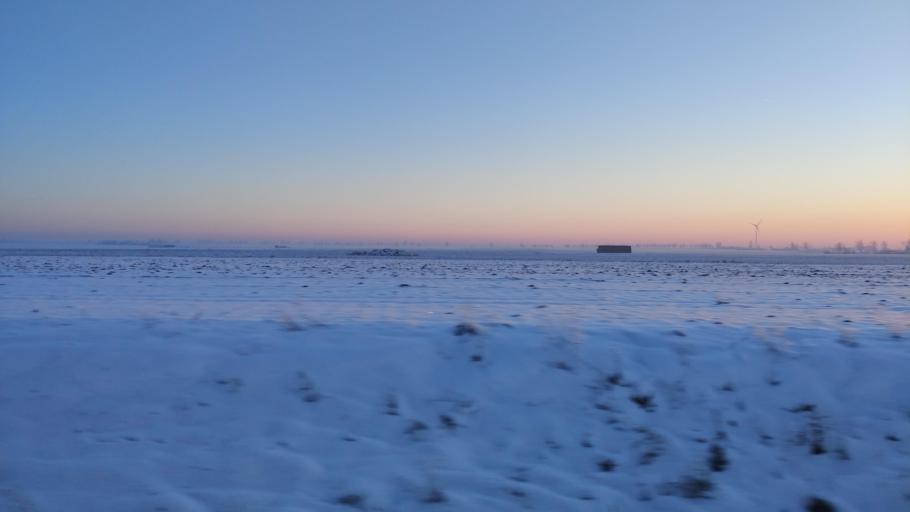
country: PL
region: Kujawsko-Pomorskie
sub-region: Powiat zninski
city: Znin
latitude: 52.8691
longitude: 17.8038
